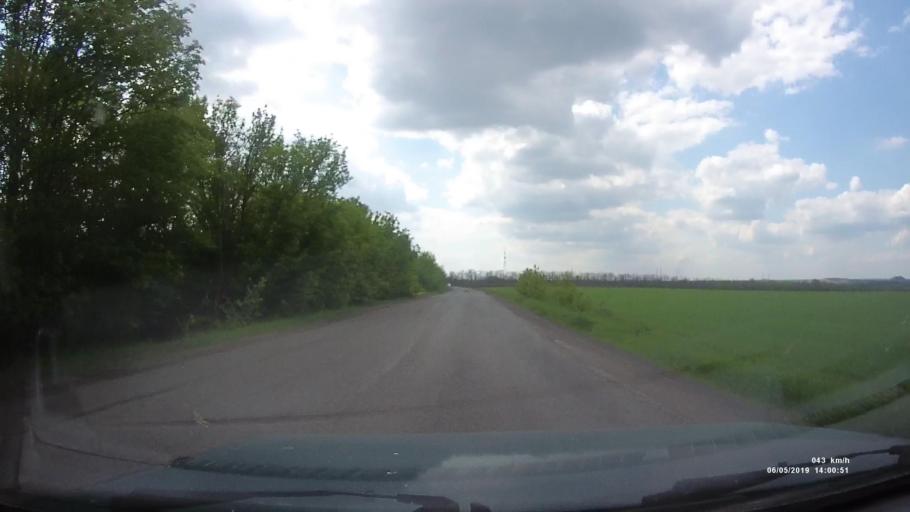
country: RU
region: Rostov
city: Shakhty
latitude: 47.6859
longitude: 40.3827
